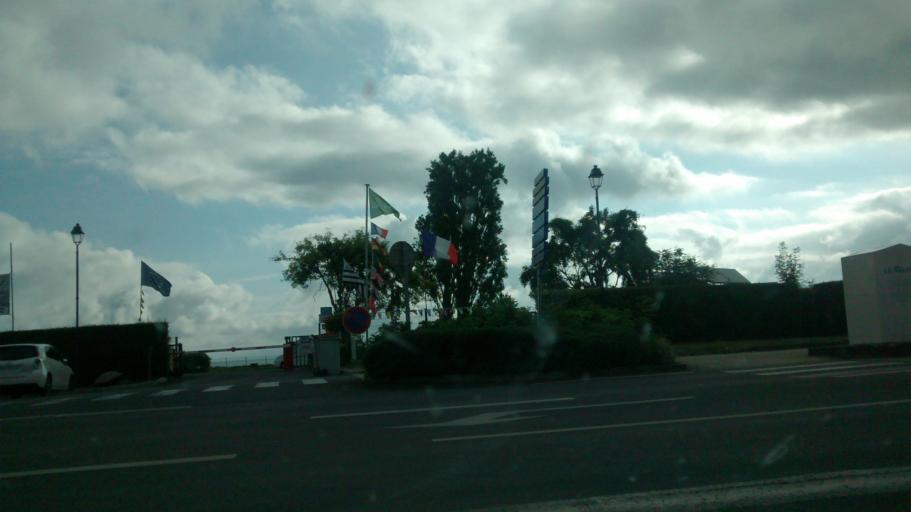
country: FR
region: Brittany
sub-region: Departement d'Ille-et-Vilaine
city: La Fresnais
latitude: 48.6189
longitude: -1.8497
